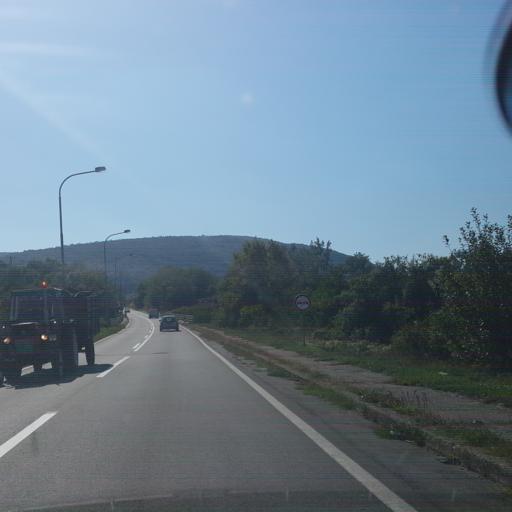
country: RS
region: Central Serbia
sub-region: Zajecarski Okrug
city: Knjazevac
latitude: 43.5510
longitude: 22.2379
